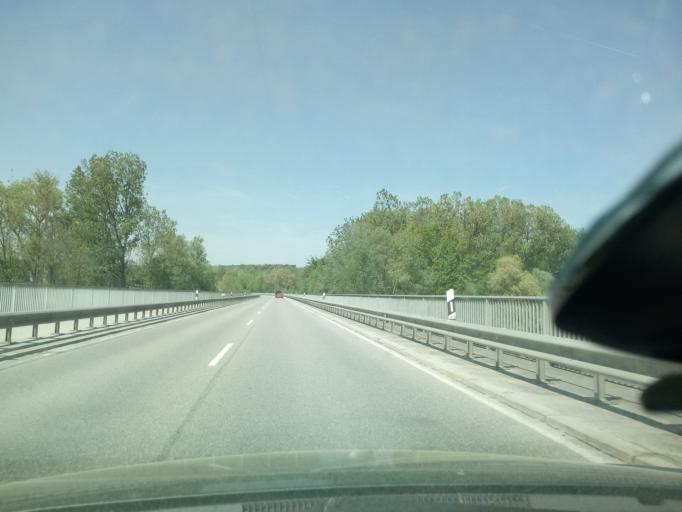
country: DE
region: Bavaria
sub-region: Upper Bavaria
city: Kraiburg am Inn
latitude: 48.1928
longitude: 12.4325
